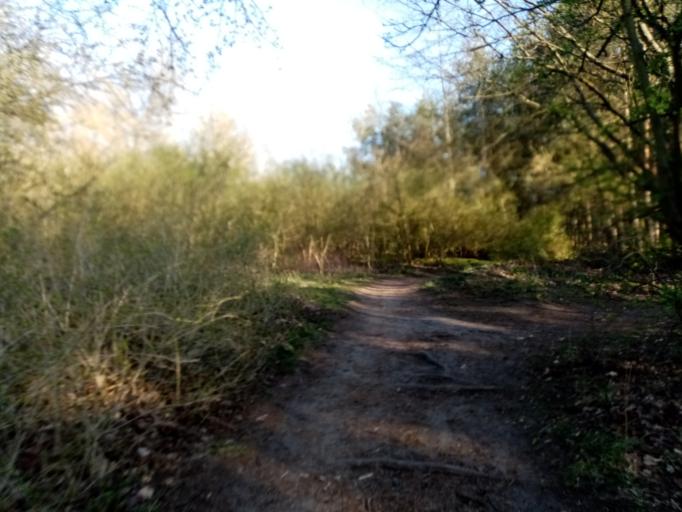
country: DE
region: Berlin
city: Karlshorst
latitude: 52.4728
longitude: 13.5388
